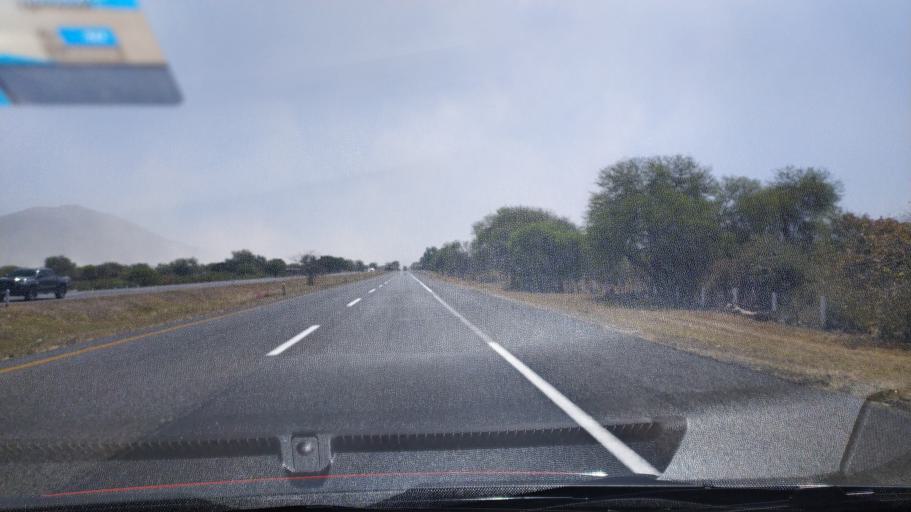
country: MX
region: Jalisco
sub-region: Acatlan de Juarez
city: Villa de los Ninos
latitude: 20.3371
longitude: -103.5709
